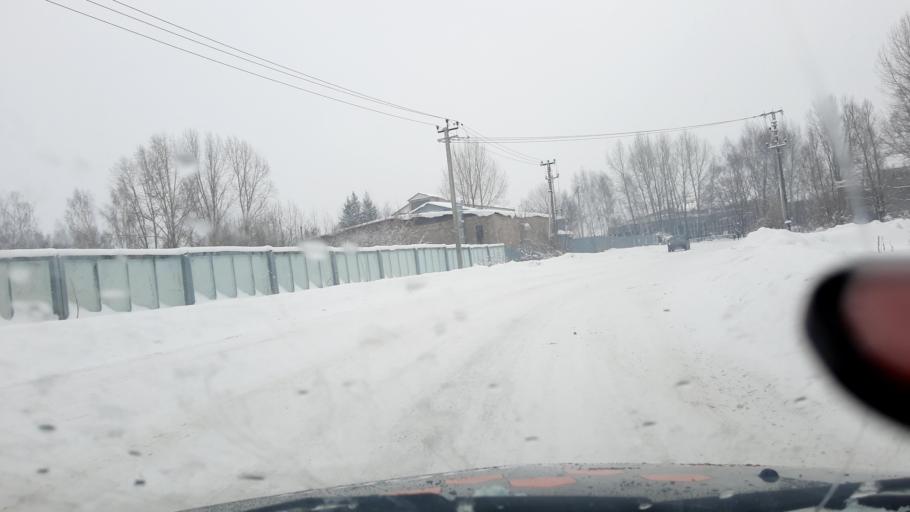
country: RU
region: Bashkortostan
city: Blagoveshchensk
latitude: 55.0326
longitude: 56.0183
